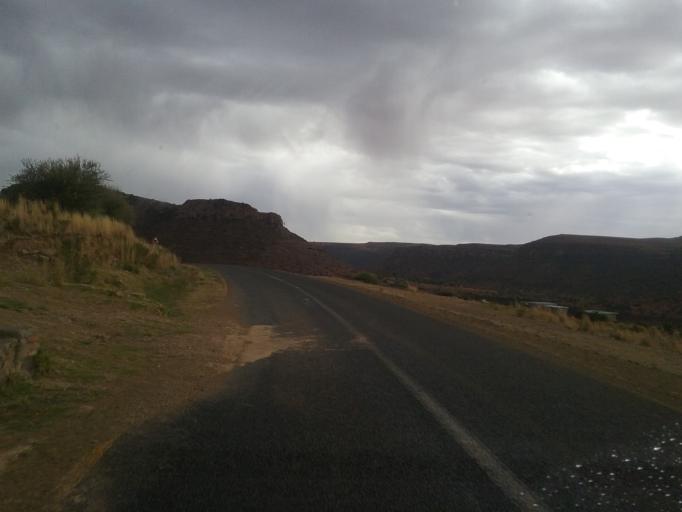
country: LS
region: Quthing
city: Quthing
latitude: -30.3119
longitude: 27.7383
